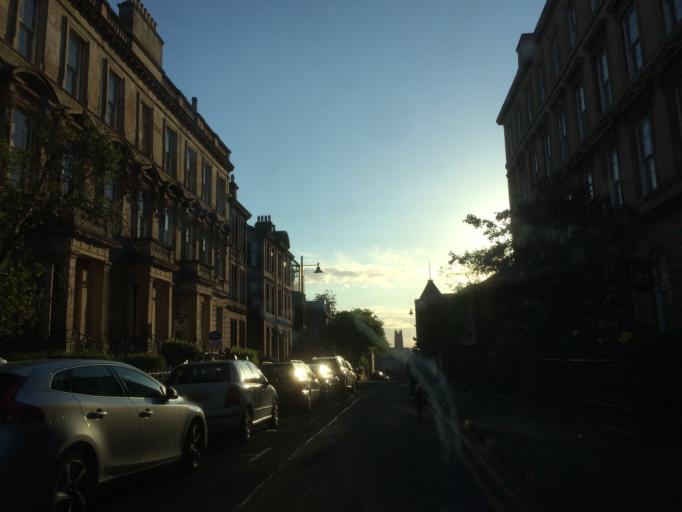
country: GB
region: Scotland
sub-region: Glasgow City
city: Glasgow
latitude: 55.8672
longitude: -4.2658
